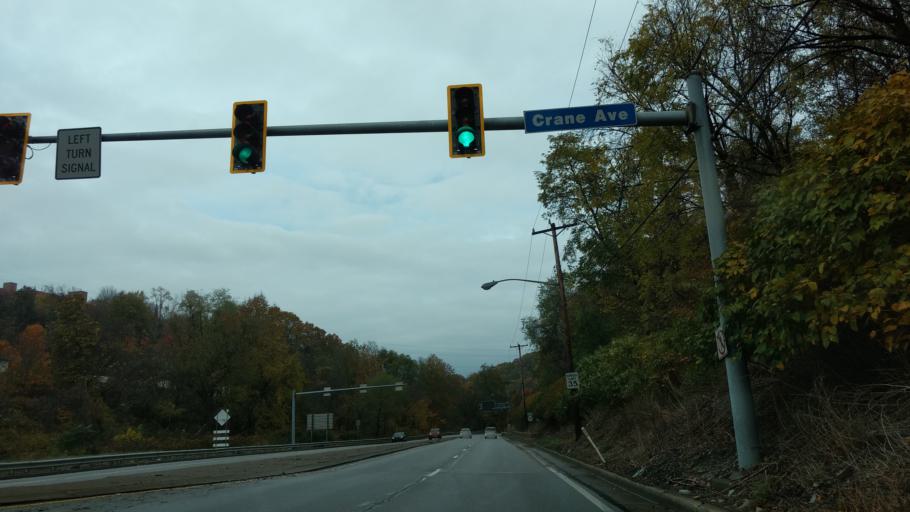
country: US
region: Pennsylvania
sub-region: Allegheny County
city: Mount Oliver
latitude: 40.4171
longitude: -80.0146
